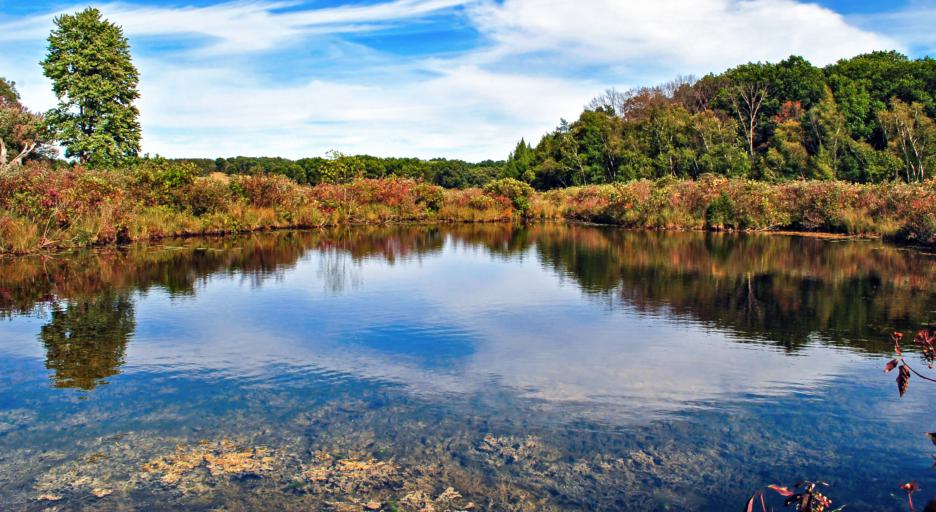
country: US
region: Wisconsin
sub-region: Marquette County
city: Montello
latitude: 43.6881
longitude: -89.3961
